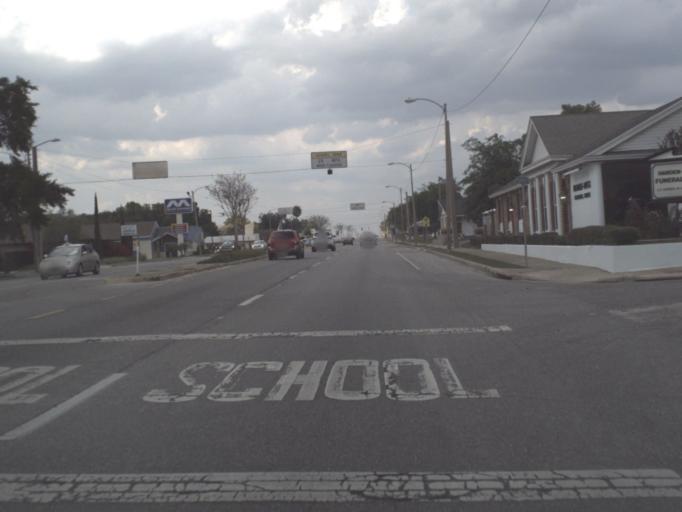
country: US
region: Florida
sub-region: Lake County
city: Eustis
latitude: 28.8372
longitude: -81.6854
